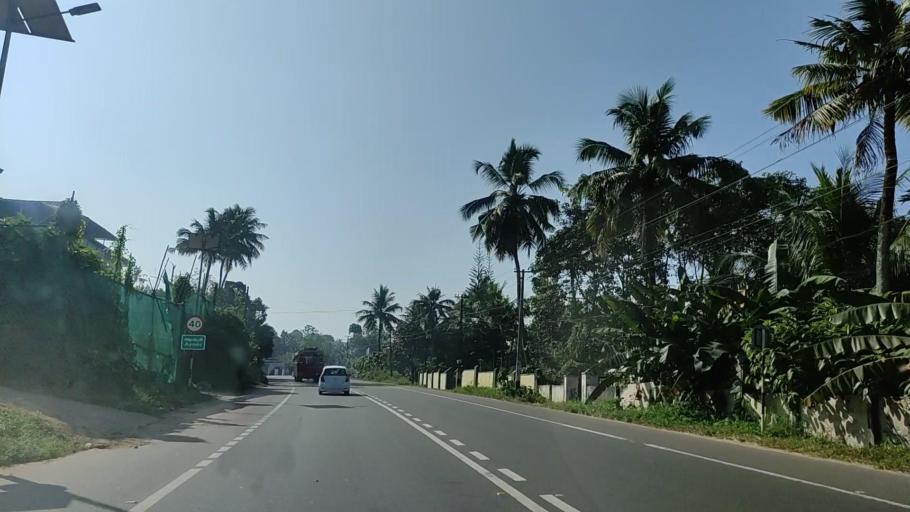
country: IN
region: Kerala
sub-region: Kollam
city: Punalur
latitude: 8.9028
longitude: 76.8560
